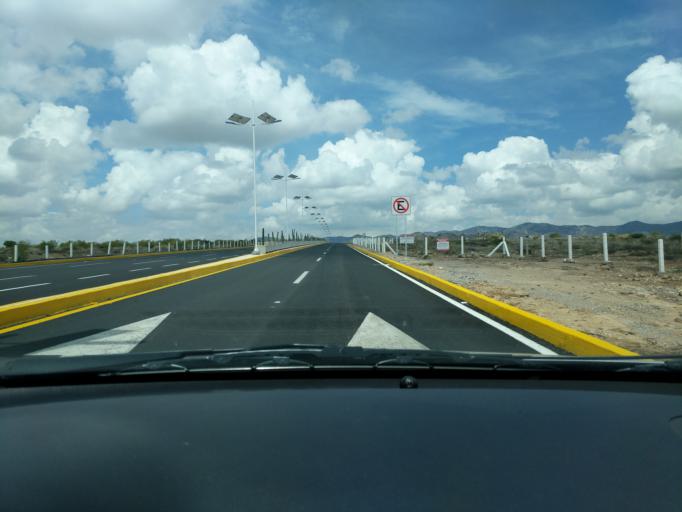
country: MX
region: San Luis Potosi
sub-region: Mexquitic de Carmona
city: Guadalupe Victoria
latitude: 22.1655
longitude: -101.0534
